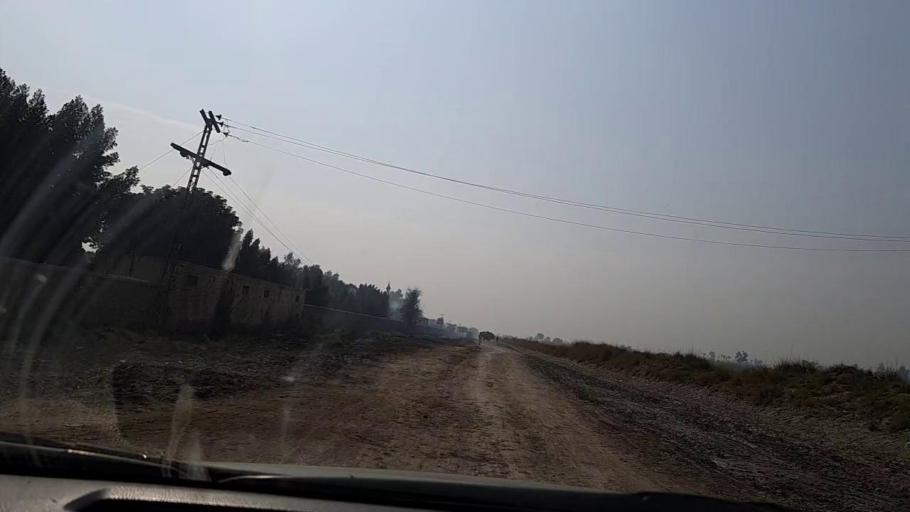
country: PK
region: Sindh
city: Daulatpur
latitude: 26.5570
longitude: 67.9836
